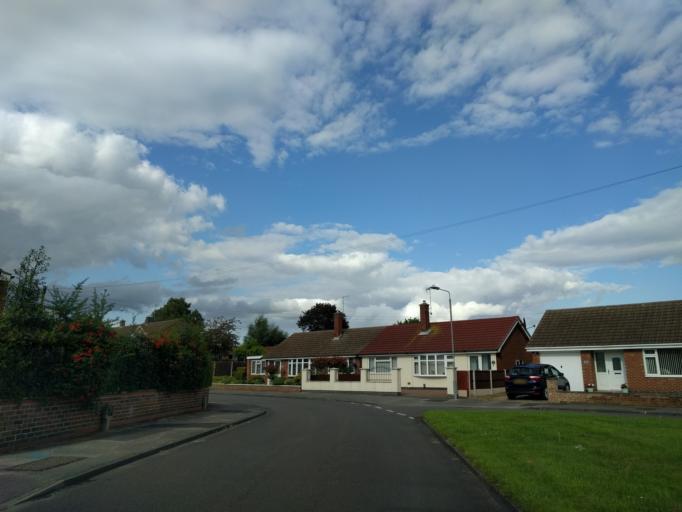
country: GB
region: England
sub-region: Nottinghamshire
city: Newark on Trent
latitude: 53.0610
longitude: -0.7797
